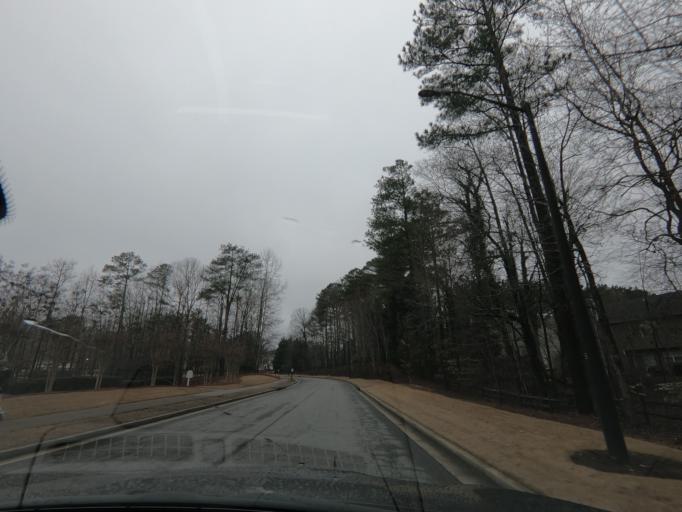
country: US
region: Georgia
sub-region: Cobb County
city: Kennesaw
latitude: 34.0557
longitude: -84.6323
